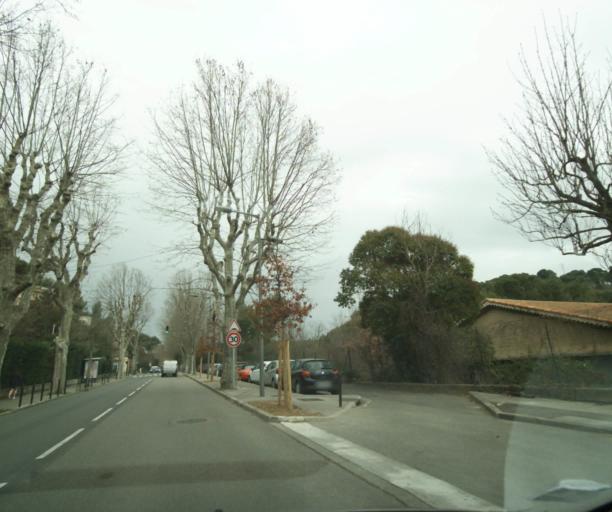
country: FR
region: Provence-Alpes-Cote d'Azur
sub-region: Departement des Bouches-du-Rhone
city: Aix-en-Provence
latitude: 43.5354
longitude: 5.4578
